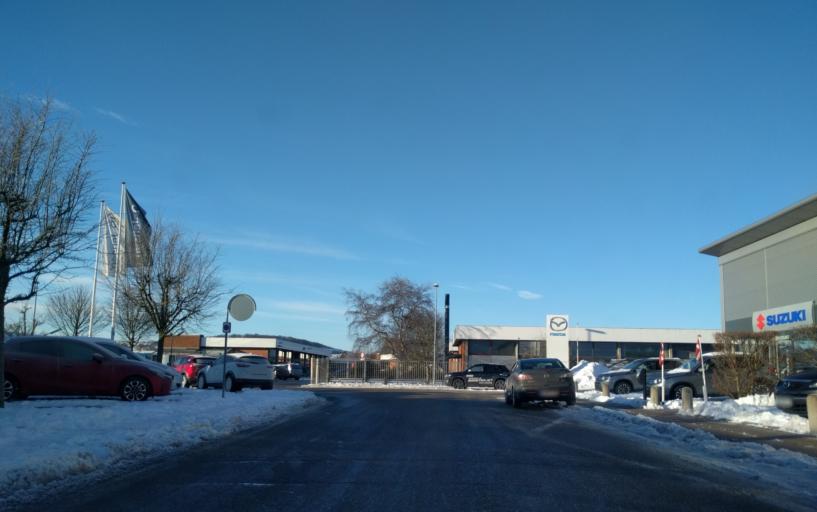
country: DK
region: North Denmark
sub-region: Alborg Kommune
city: Aalborg
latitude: 57.0345
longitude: 9.9237
